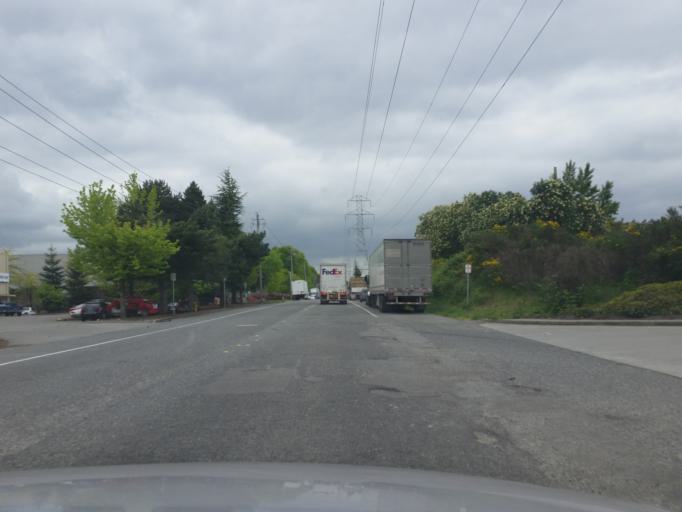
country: US
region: Washington
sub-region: King County
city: Bellevue
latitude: 47.6245
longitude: -122.1751
